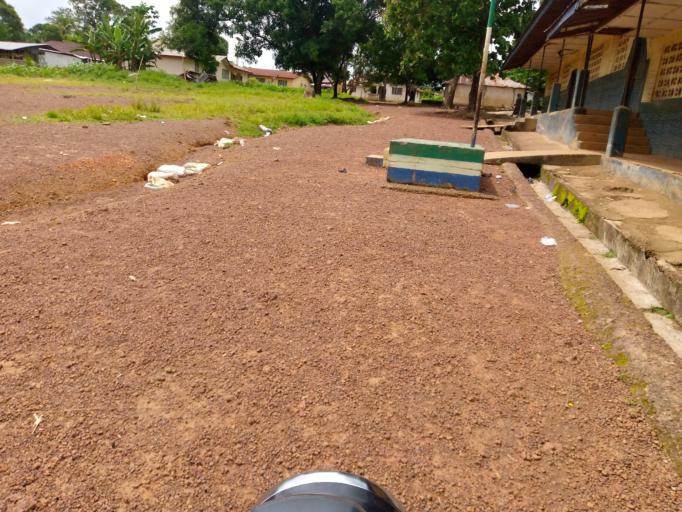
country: SL
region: Southern Province
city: Moyamba
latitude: 8.1545
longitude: -12.4332
